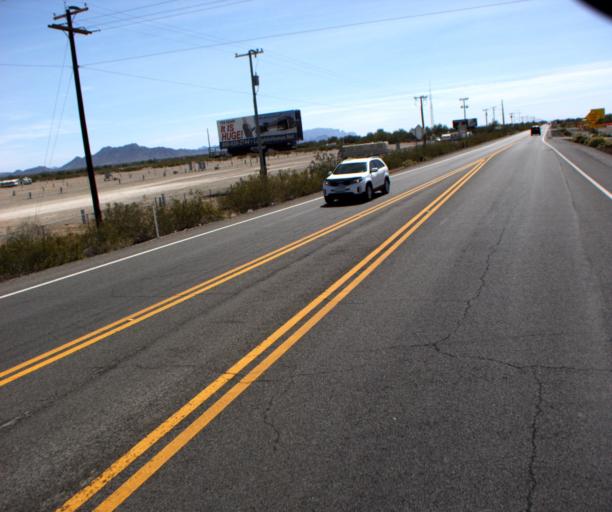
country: US
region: Arizona
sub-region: La Paz County
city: Quartzsite
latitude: 33.6593
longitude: -114.2171
